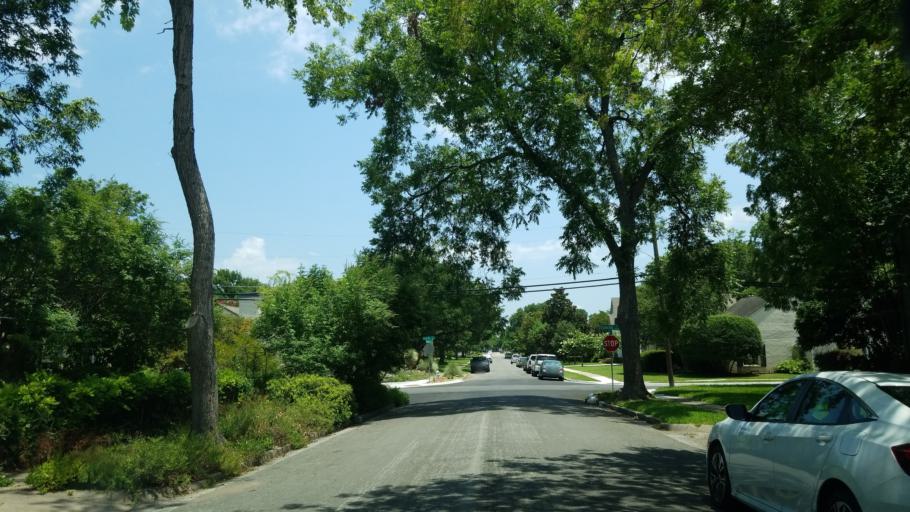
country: US
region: Texas
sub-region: Dallas County
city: Highland Park
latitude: 32.8308
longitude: -96.7647
